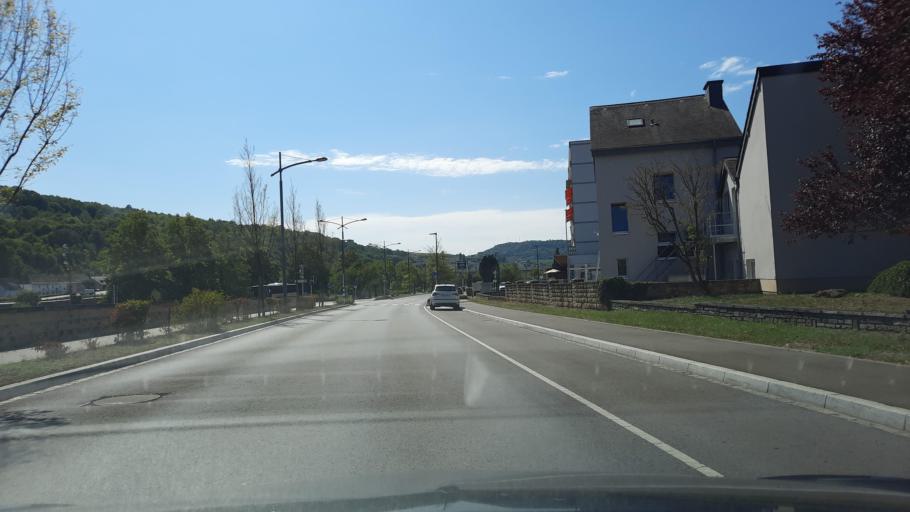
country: LU
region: Grevenmacher
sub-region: Canton de Grevenmacher
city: Grevenmacher
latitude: 49.6796
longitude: 6.4467
